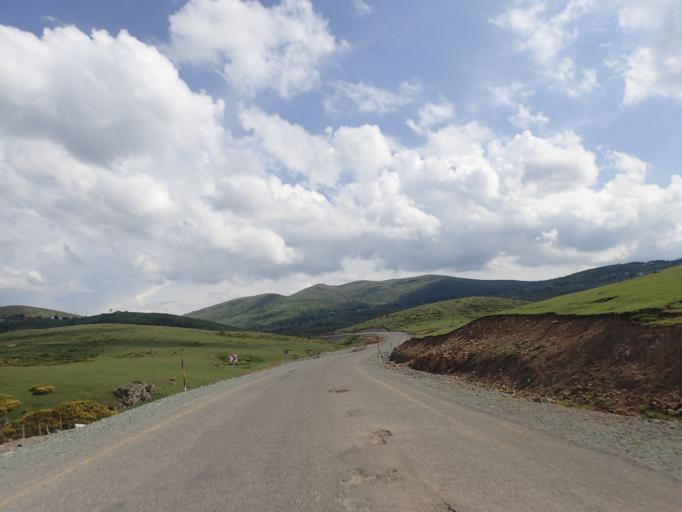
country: TR
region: Ordu
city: Topcam
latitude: 40.6840
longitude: 37.9293
